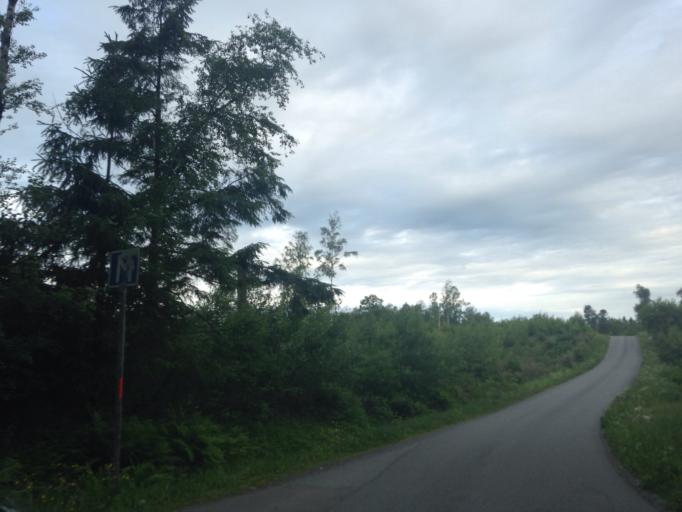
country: SE
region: Vaestra Goetaland
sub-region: Goteborg
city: Torslanda
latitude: 57.7775
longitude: 11.8534
